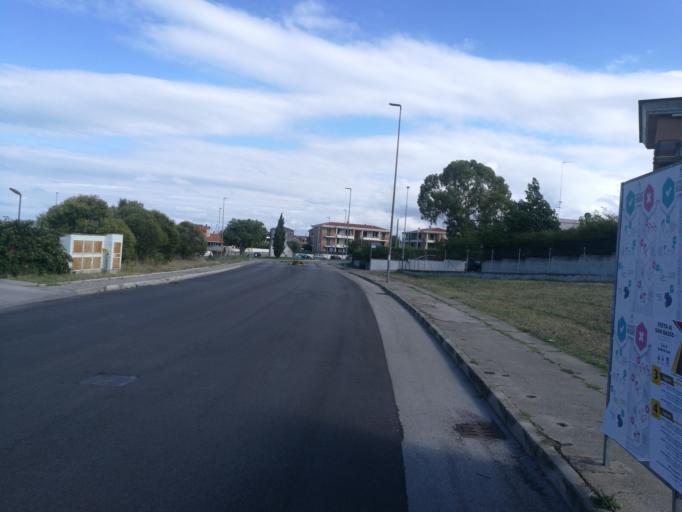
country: IT
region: Molise
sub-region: Provincia di Campobasso
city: Termoli
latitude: 41.9818
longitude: 14.9840
